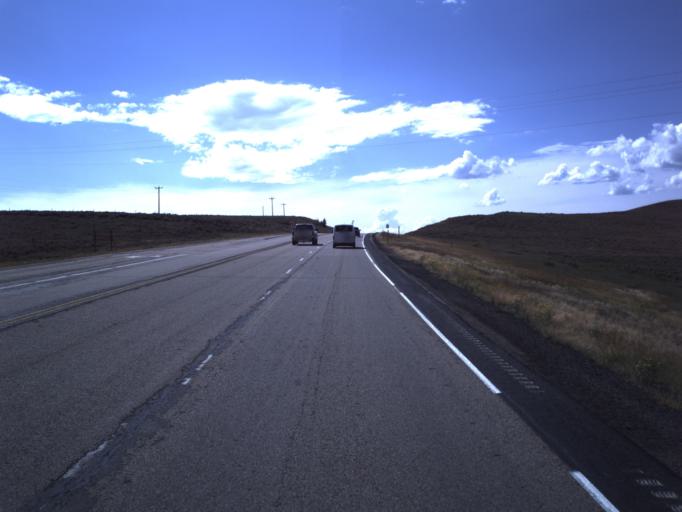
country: US
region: Utah
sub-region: Summit County
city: Francis
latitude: 40.1833
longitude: -111.0523
